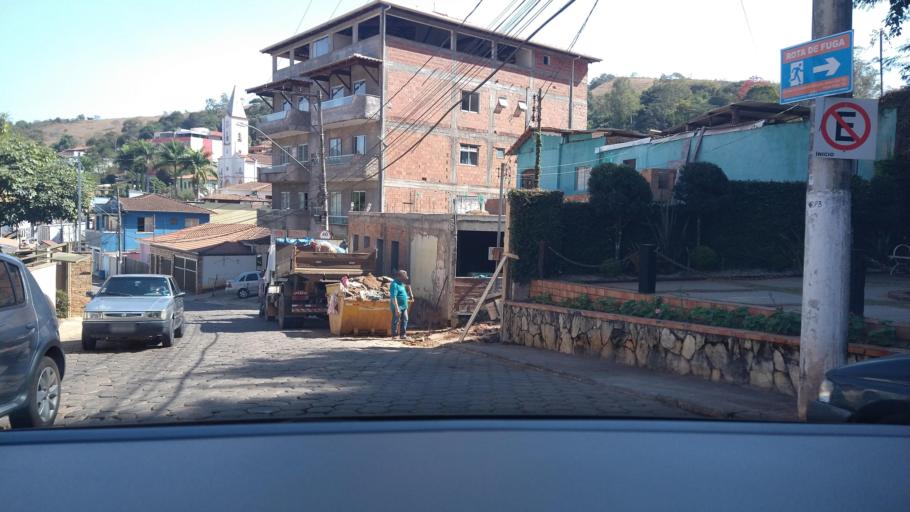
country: BR
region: Minas Gerais
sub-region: Rio Piracicaba
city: Rio Piracicaba
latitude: -19.9268
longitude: -43.1699
